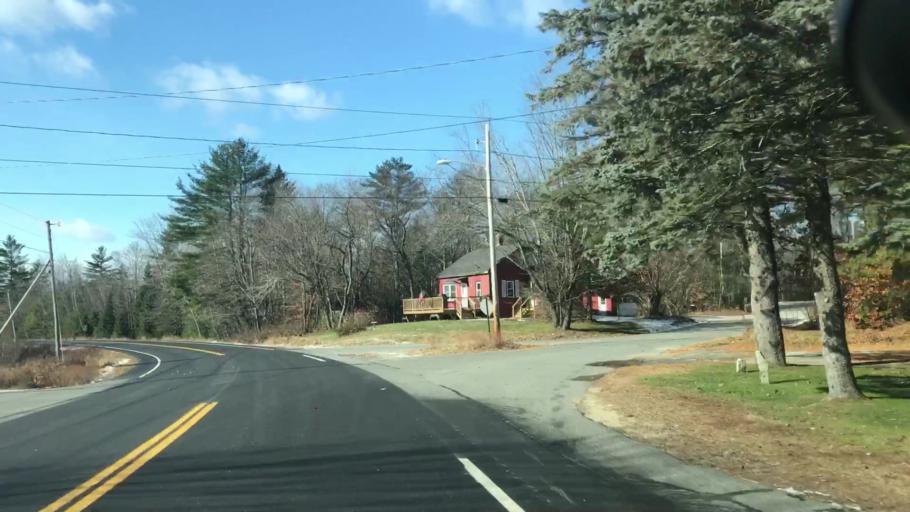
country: US
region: Maine
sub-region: Oxford County
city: Porter
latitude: 43.7956
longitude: -70.9418
